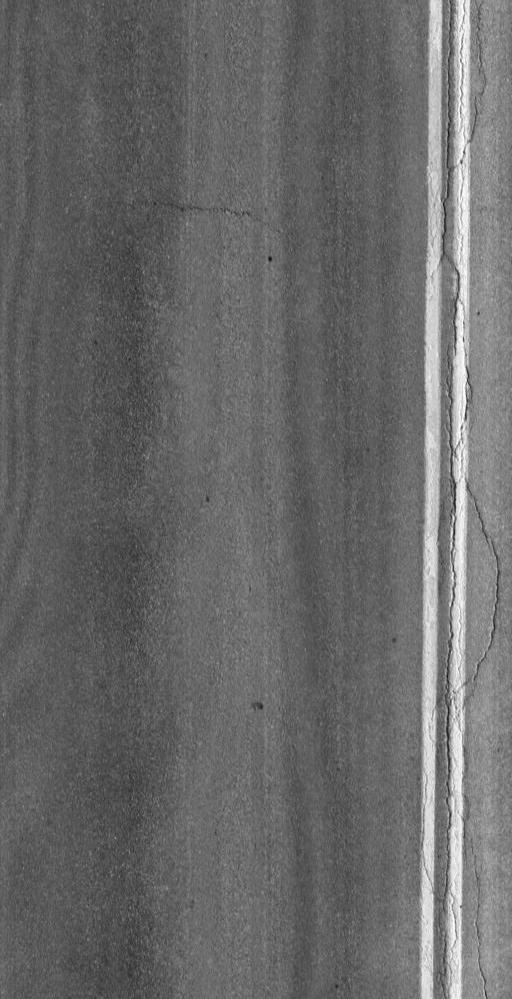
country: US
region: Vermont
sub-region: Chittenden County
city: Burlington
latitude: 44.3673
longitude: -73.2239
